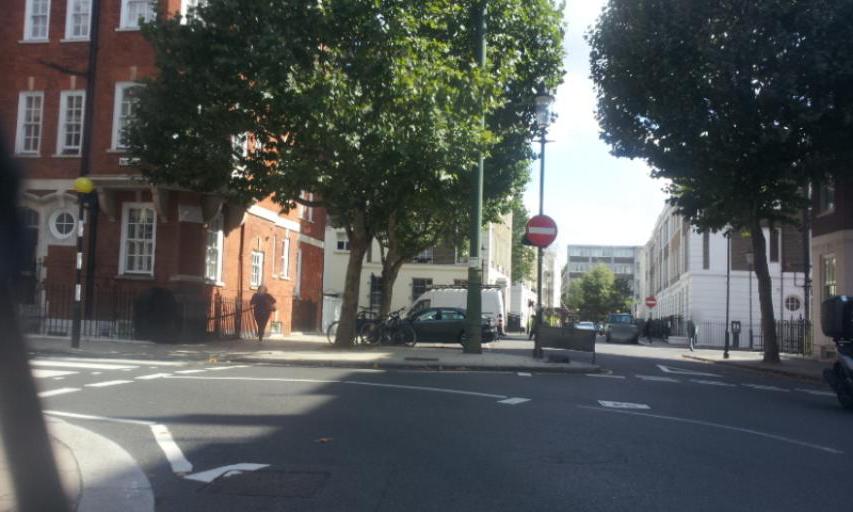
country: GB
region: England
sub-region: Greater London
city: Chelsea
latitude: 51.4911
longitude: -0.1633
